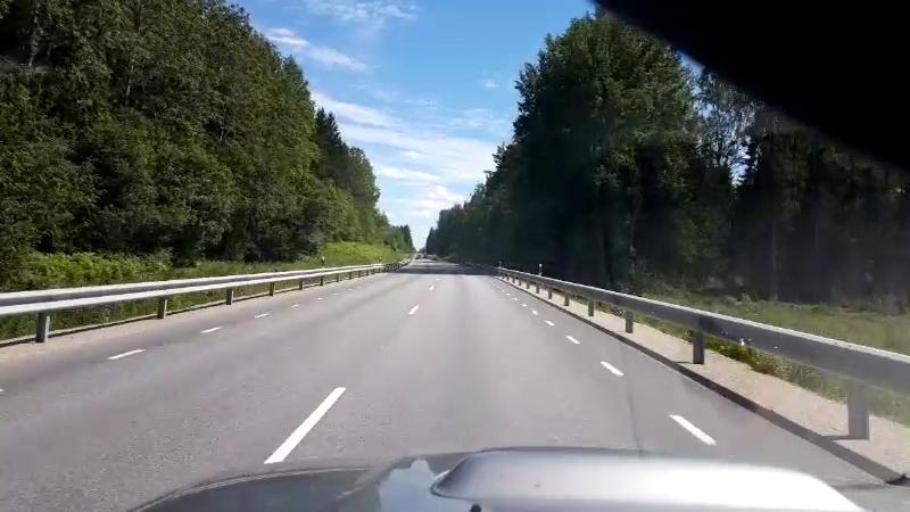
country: EE
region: Jogevamaa
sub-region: Jogeva linn
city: Jogeva
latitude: 58.7873
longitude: 26.3129
